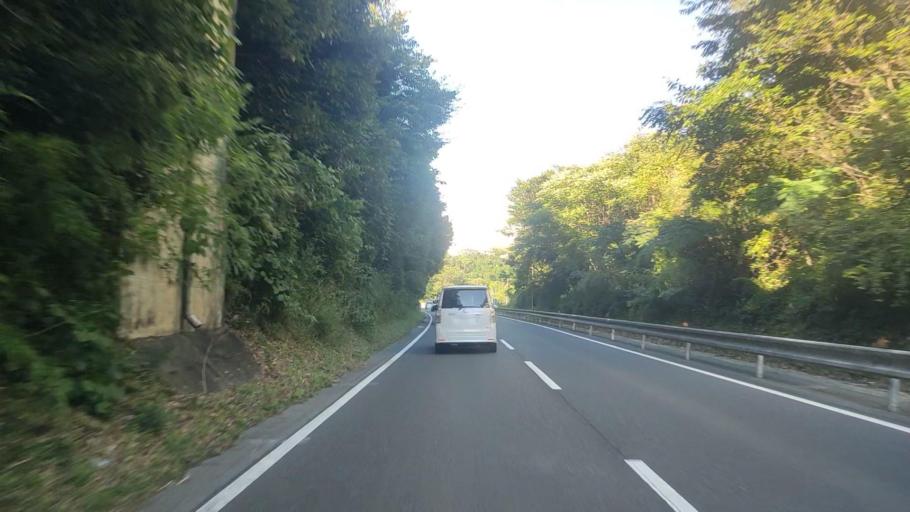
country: JP
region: Shiga Prefecture
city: Hino
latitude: 34.9930
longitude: 136.2329
